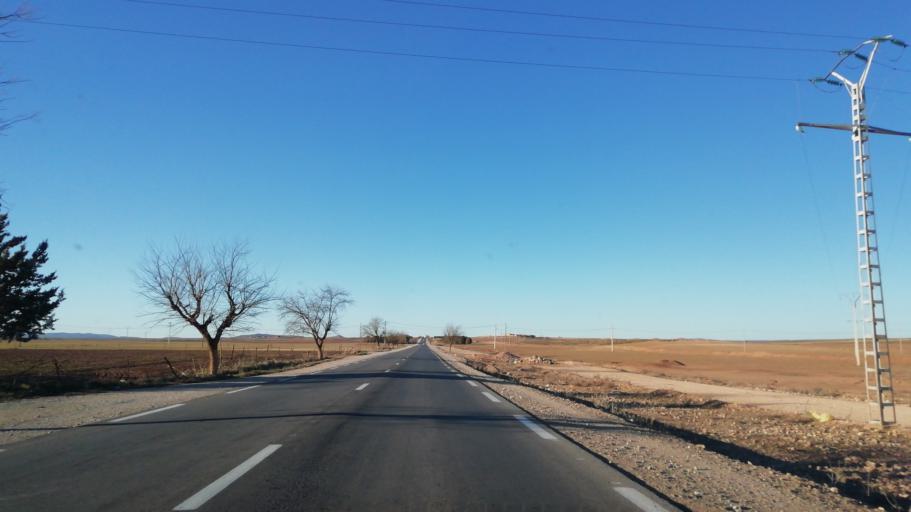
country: DZ
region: Tlemcen
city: Sebdou
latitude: 34.5194
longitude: -1.2883
